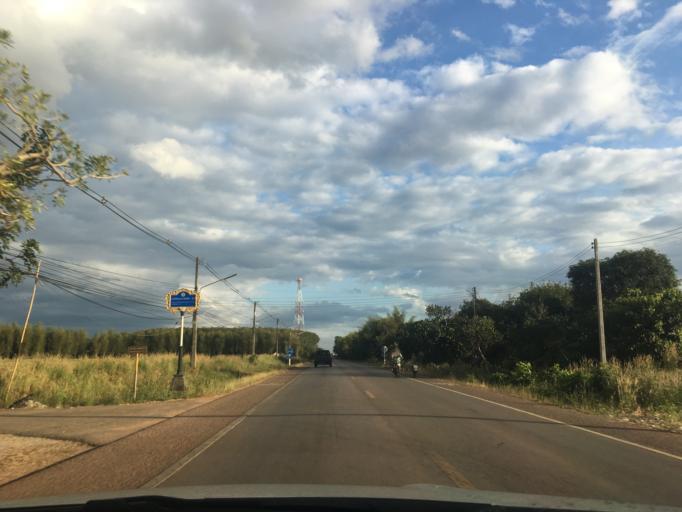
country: TH
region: Chanthaburi
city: Na Yai Am
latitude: 12.7384
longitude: 101.7407
